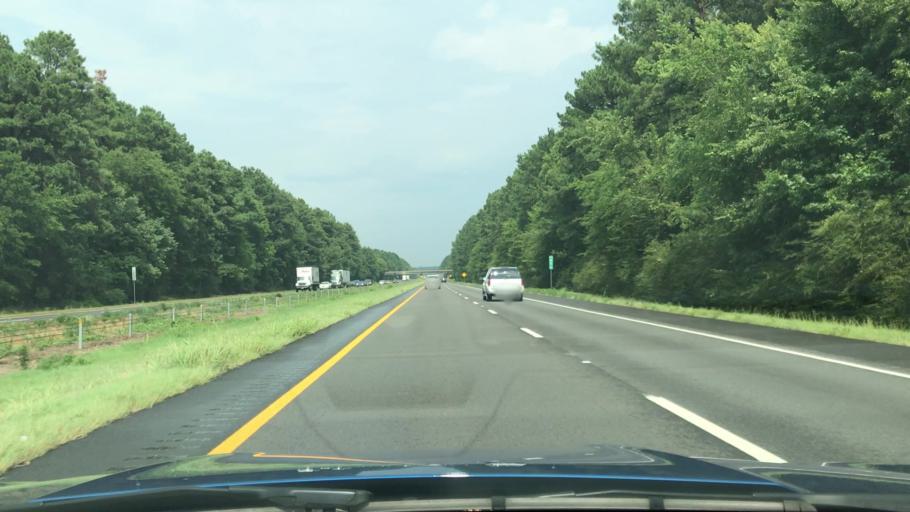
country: US
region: Texas
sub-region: Harrison County
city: Hallsville
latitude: 32.4790
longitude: -94.5512
